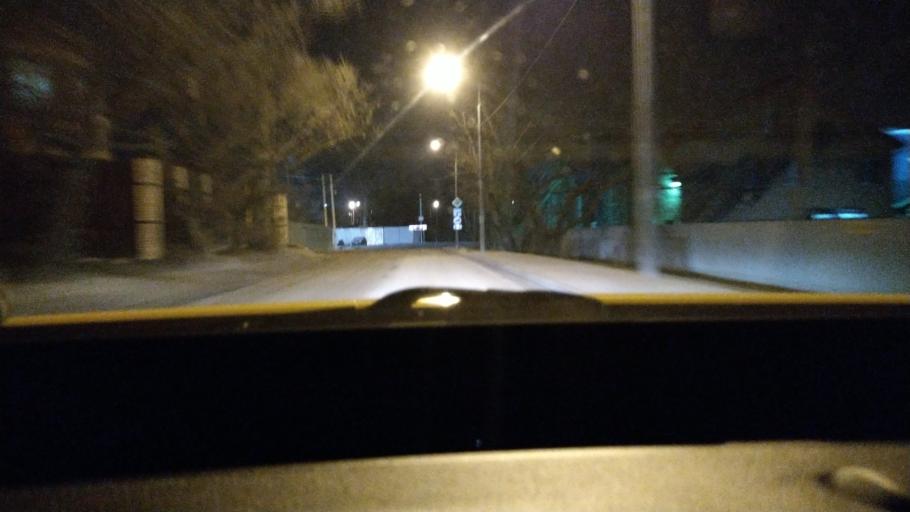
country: RU
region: Moskovskaya
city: Troitsk
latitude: 55.4425
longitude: 37.2847
